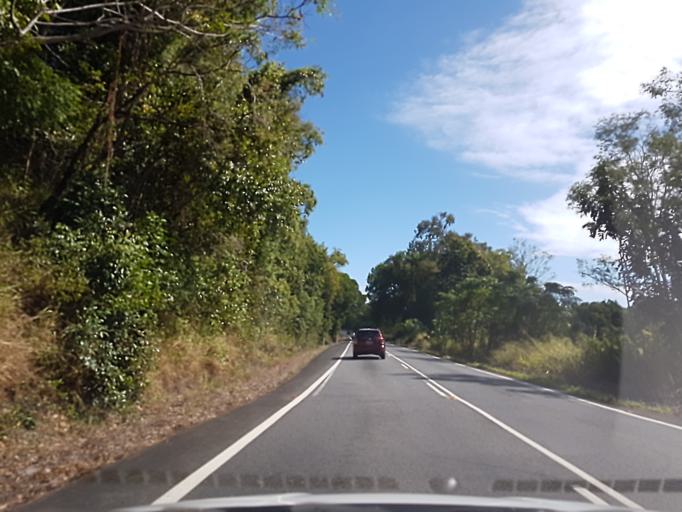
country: AU
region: Queensland
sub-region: Cairns
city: Port Douglas
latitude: -16.5644
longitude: 145.5003
